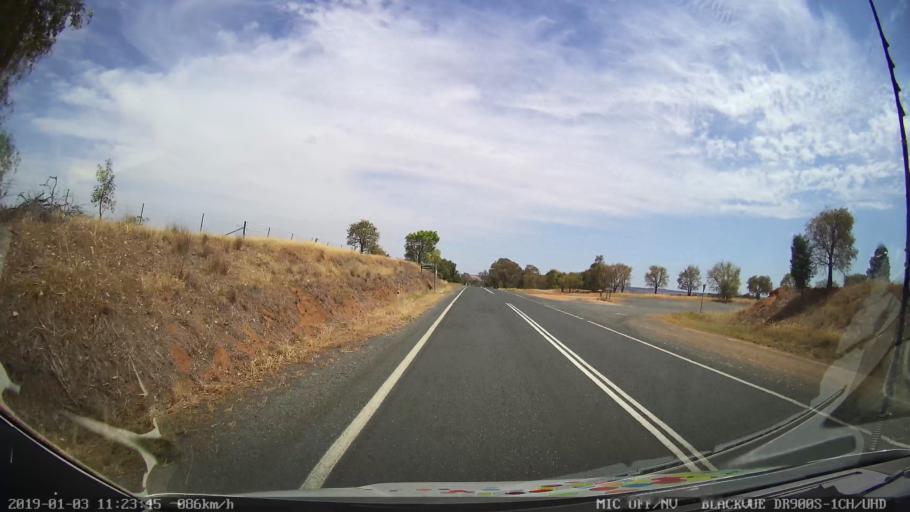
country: AU
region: New South Wales
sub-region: Weddin
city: Grenfell
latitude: -34.0596
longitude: 148.2403
